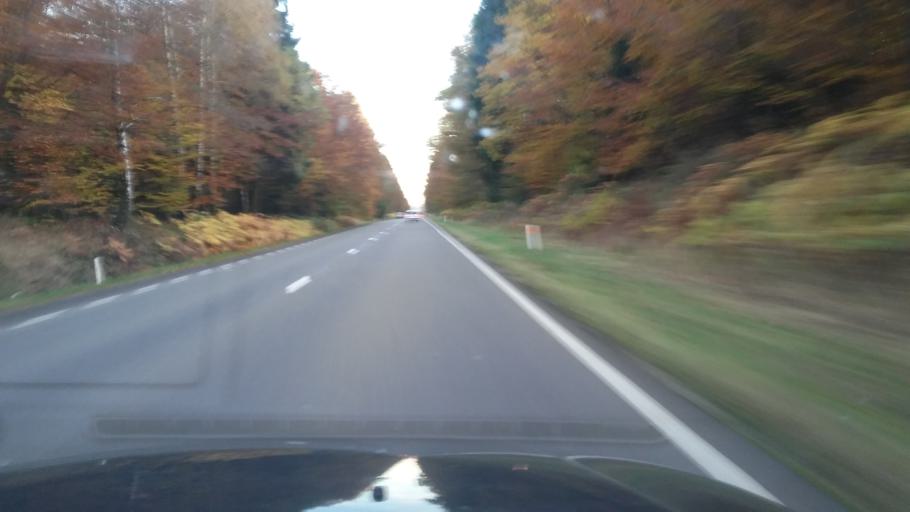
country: BE
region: Wallonia
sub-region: Province du Luxembourg
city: Herbeumont
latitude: 49.7527
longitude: 5.2060
